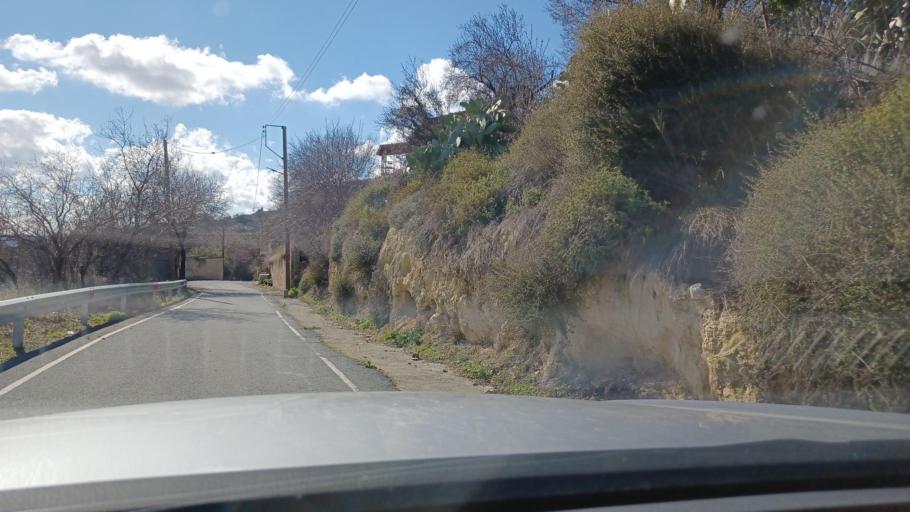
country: CY
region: Limassol
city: Pachna
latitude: 34.8256
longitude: 32.8076
